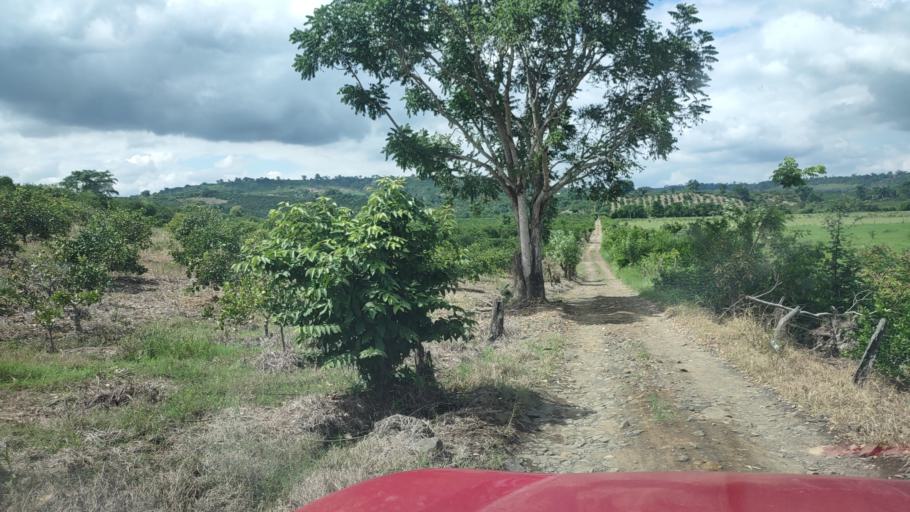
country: MX
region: Puebla
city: San Jose Acateno
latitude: 20.2201
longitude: -97.1431
